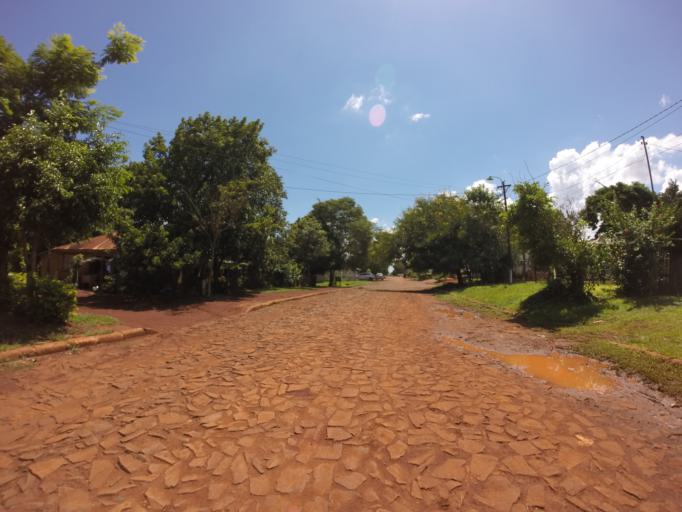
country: PY
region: Alto Parana
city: Ciudad del Este
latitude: -25.3978
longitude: -54.6365
